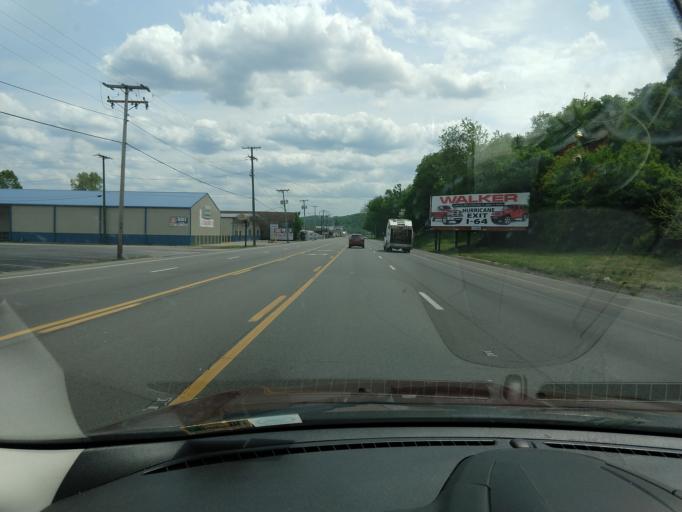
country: US
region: West Virginia
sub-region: Kanawha County
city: Dunbar
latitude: 38.3667
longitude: -81.7644
